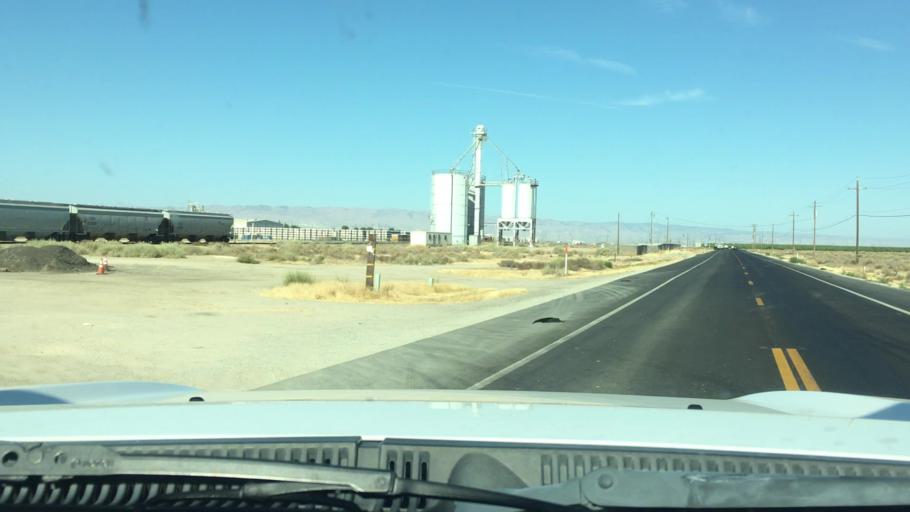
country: US
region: California
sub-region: Kern County
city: Buttonwillow
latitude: 35.3993
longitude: -119.4032
